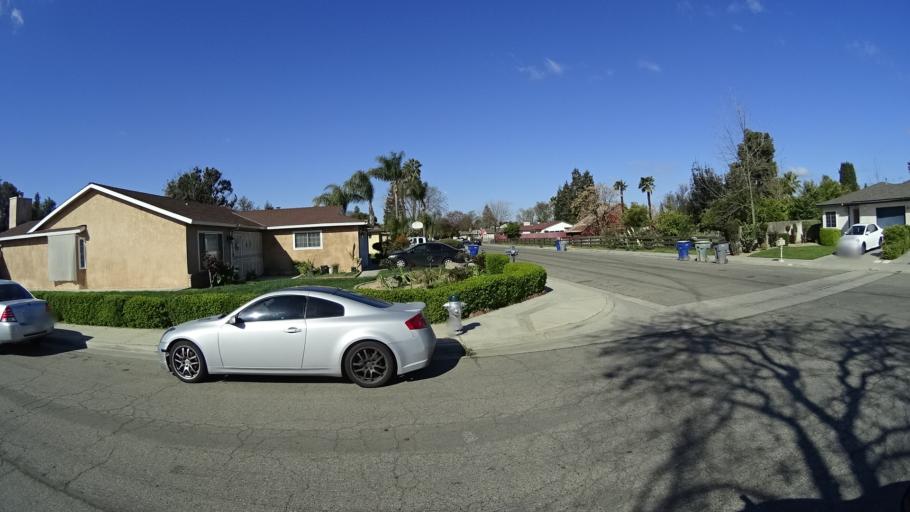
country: US
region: California
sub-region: Fresno County
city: West Park
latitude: 36.7955
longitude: -119.8814
